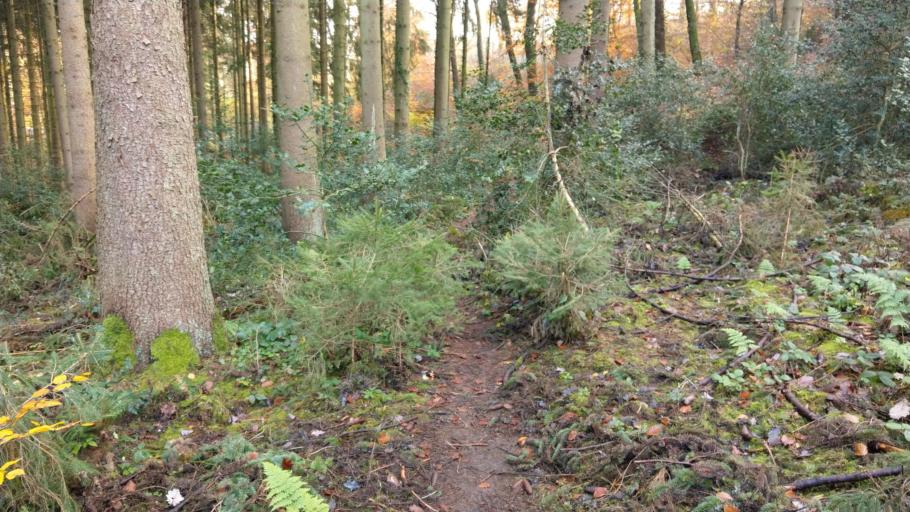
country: DE
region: North Rhine-Westphalia
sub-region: Regierungsbezirk Koln
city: Aachen
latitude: 50.7406
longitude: 6.0739
